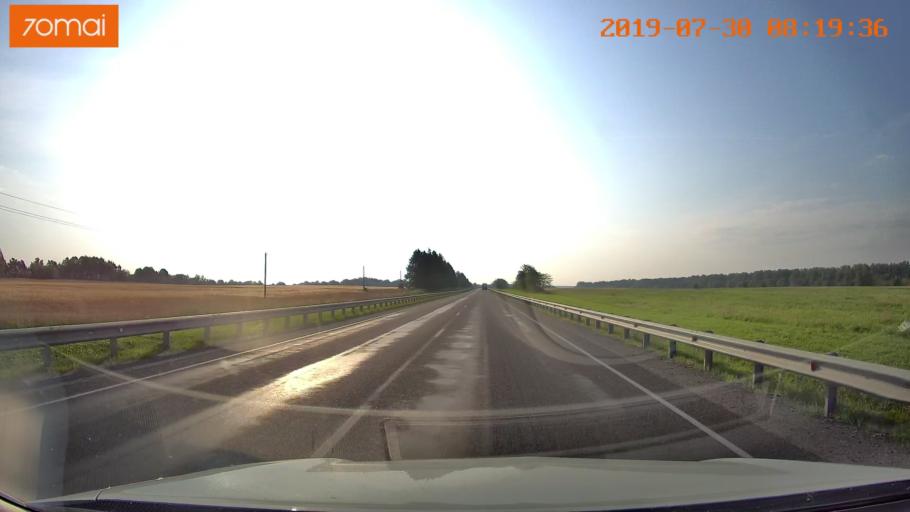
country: RU
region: Kaliningrad
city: Chernyakhovsk
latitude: 54.6277
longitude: 21.4957
